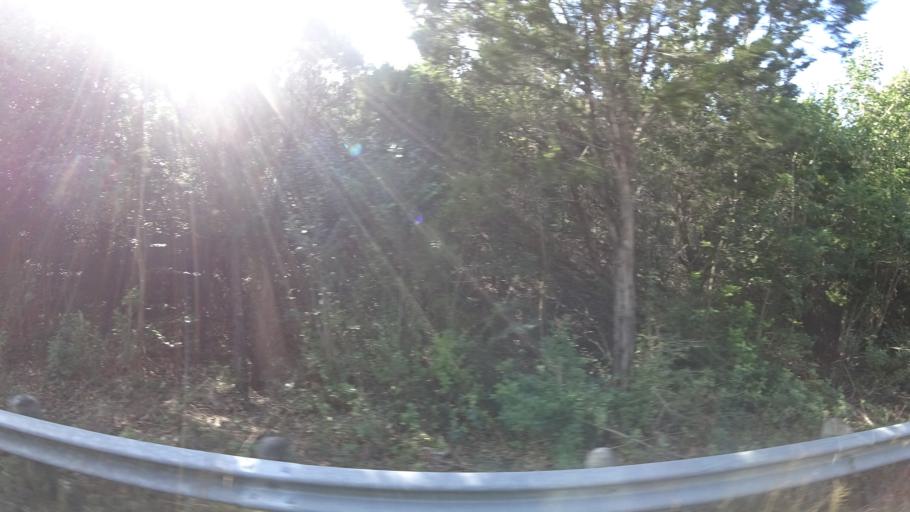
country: US
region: Texas
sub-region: Travis County
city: Lost Creek
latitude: 30.3164
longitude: -97.8646
